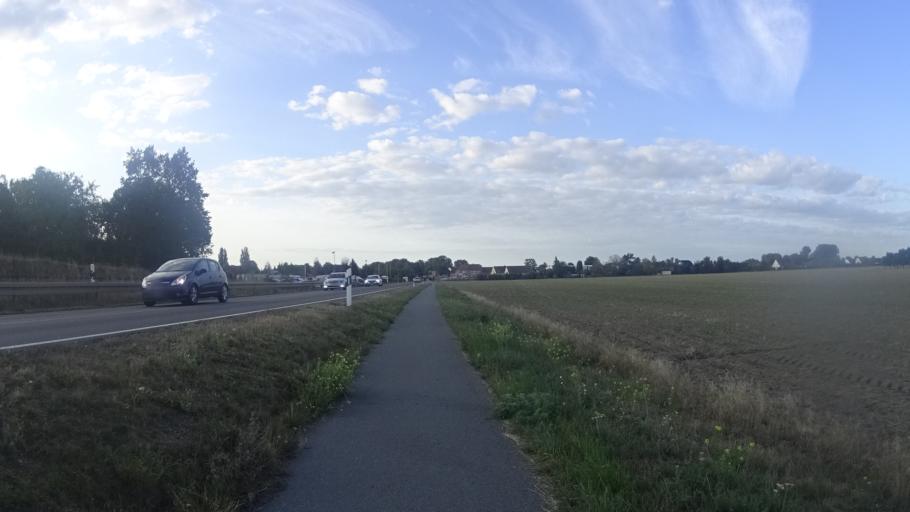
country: DE
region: Brandenburg
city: Premnitz
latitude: 52.5399
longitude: 12.3264
